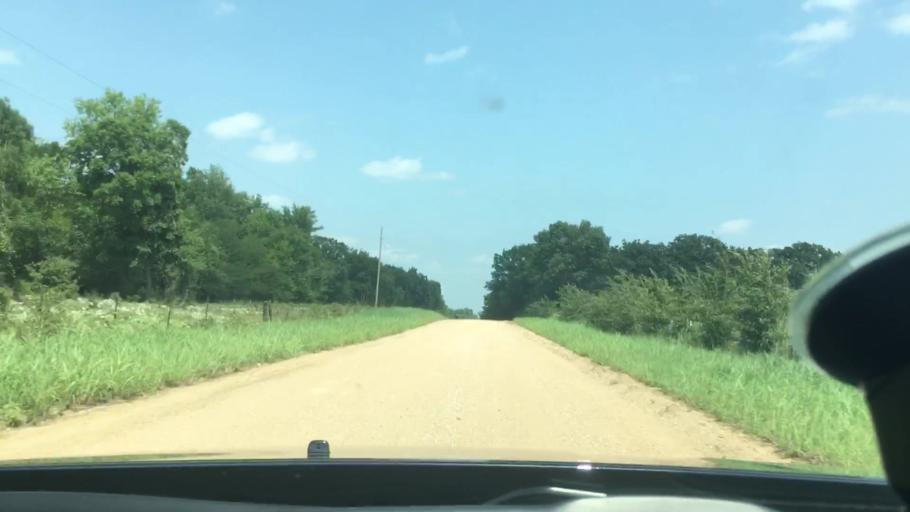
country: US
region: Oklahoma
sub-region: Coal County
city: Coalgate
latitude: 34.4251
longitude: -96.4674
